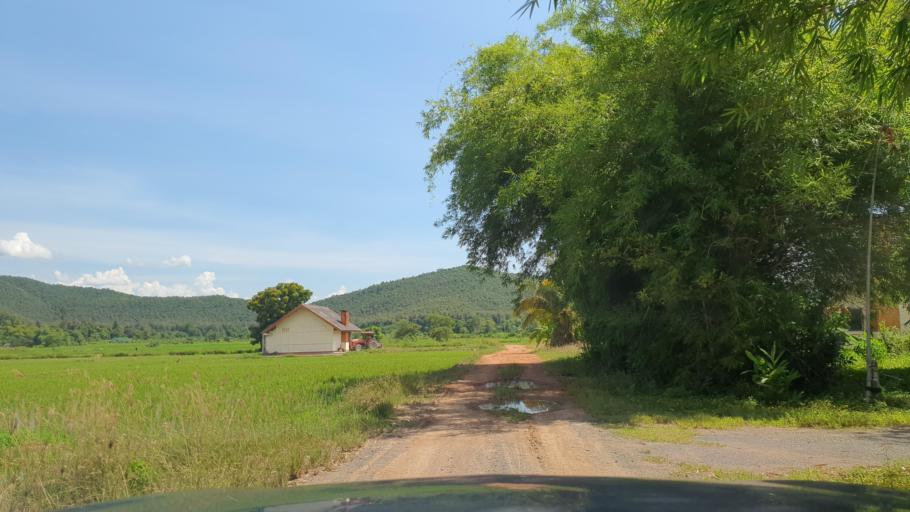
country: TH
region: Chiang Mai
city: Mae On
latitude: 18.7847
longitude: 99.1883
